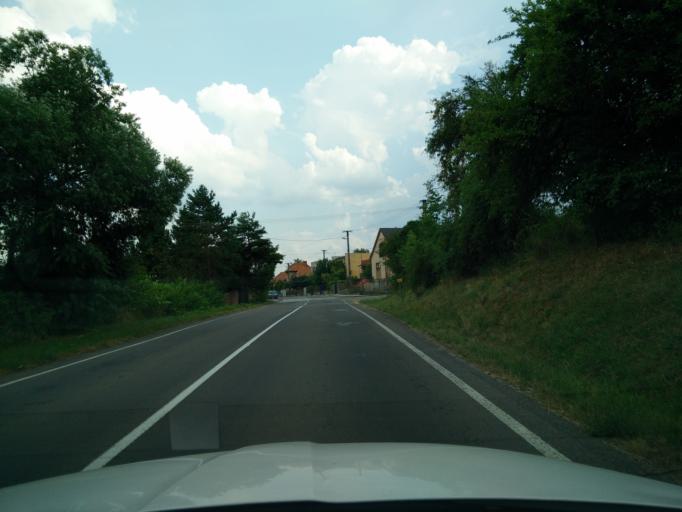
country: SK
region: Nitriansky
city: Novaky
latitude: 48.7689
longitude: 18.4914
